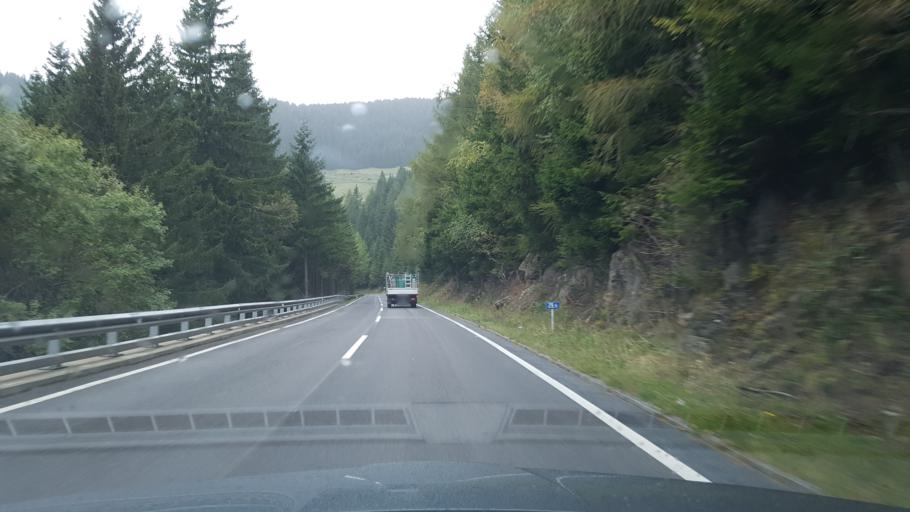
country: AT
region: Styria
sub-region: Politischer Bezirk Voitsberg
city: Salla
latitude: 47.1112
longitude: 14.9332
